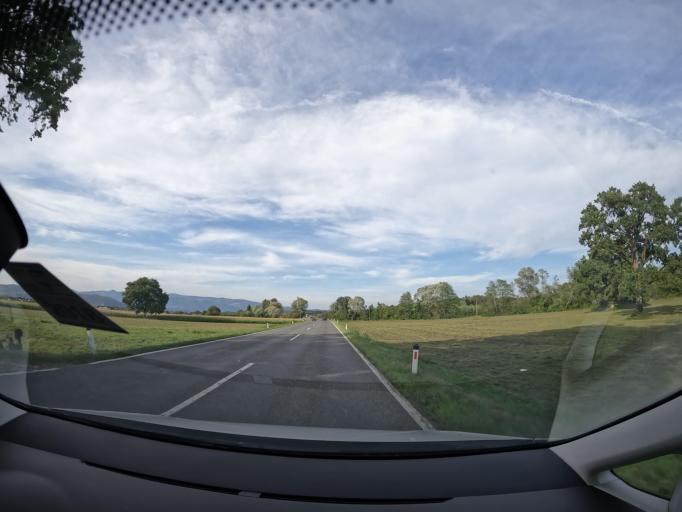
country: AT
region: Carinthia
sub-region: Politischer Bezirk Volkermarkt
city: Eberndorf
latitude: 46.6074
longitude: 14.6338
